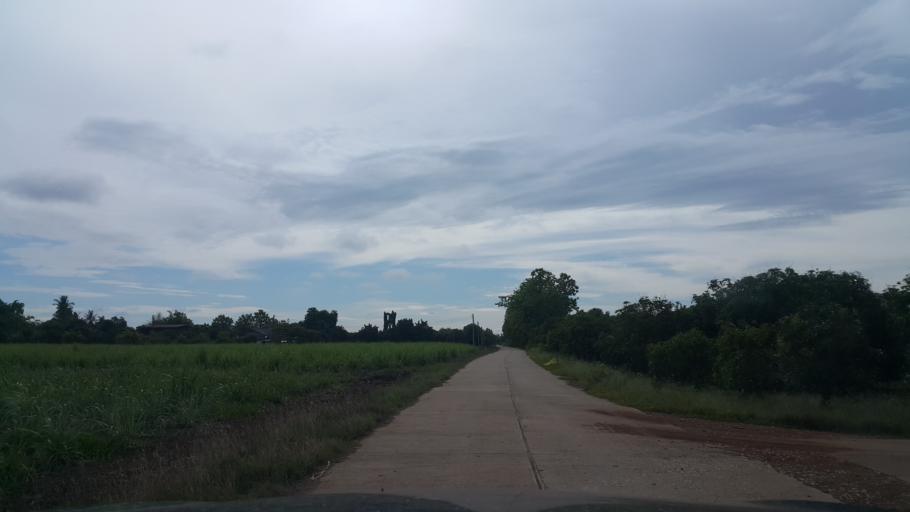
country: TH
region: Sukhothai
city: Sawankhalok
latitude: 17.2663
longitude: 99.9151
